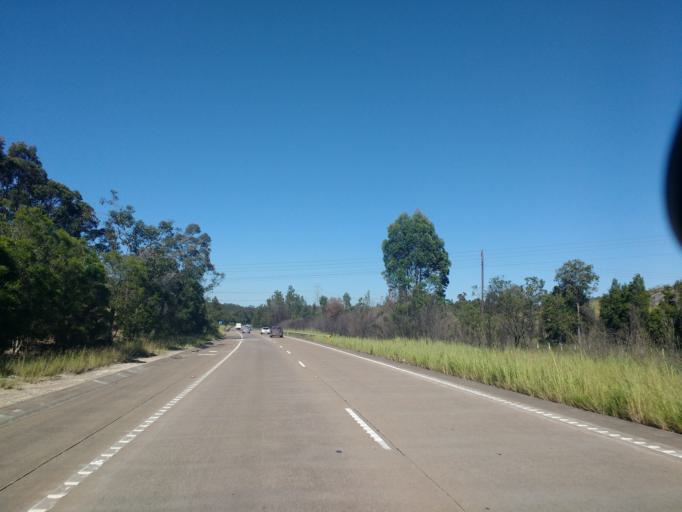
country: AU
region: New South Wales
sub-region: Lake Macquarie Shire
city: Holmesville
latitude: -32.9248
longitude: 151.5509
